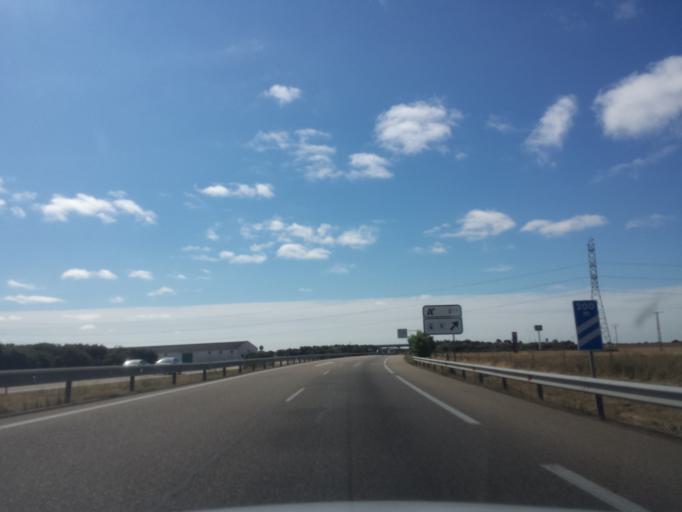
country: ES
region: Castille and Leon
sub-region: Provincia de Valladolid
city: Uruena
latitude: 41.6973
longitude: -5.2200
